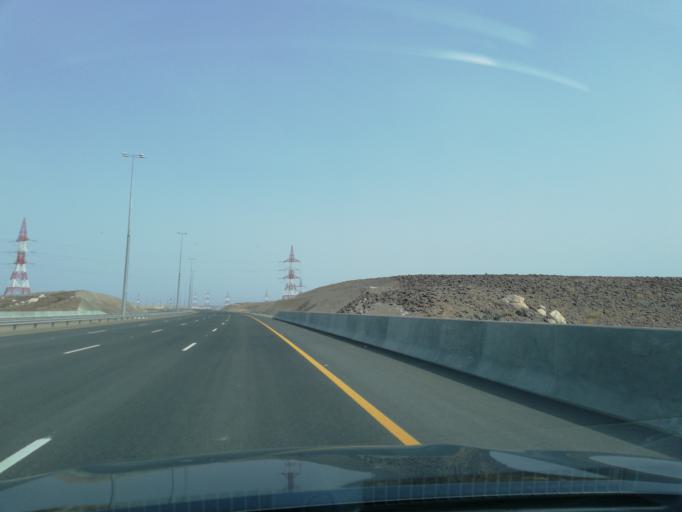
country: OM
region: Al Batinah
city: Al Sohar
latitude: 24.3361
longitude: 56.5541
